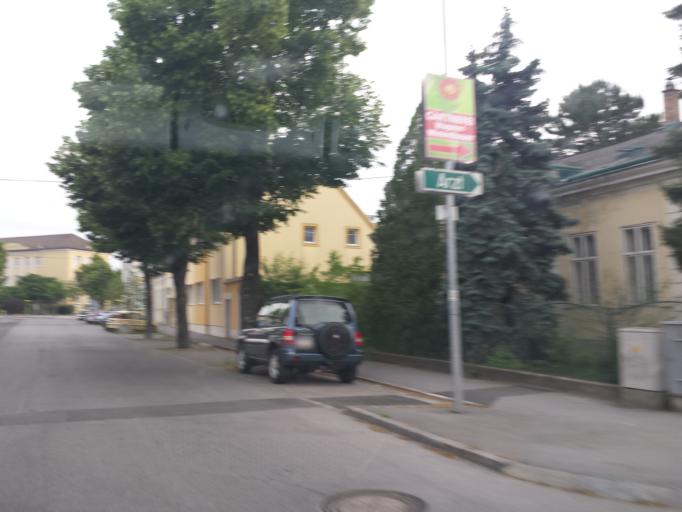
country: AT
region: Lower Austria
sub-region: Politischer Bezirk Ganserndorf
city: Deutsch-Wagram
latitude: 48.2994
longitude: 16.5604
